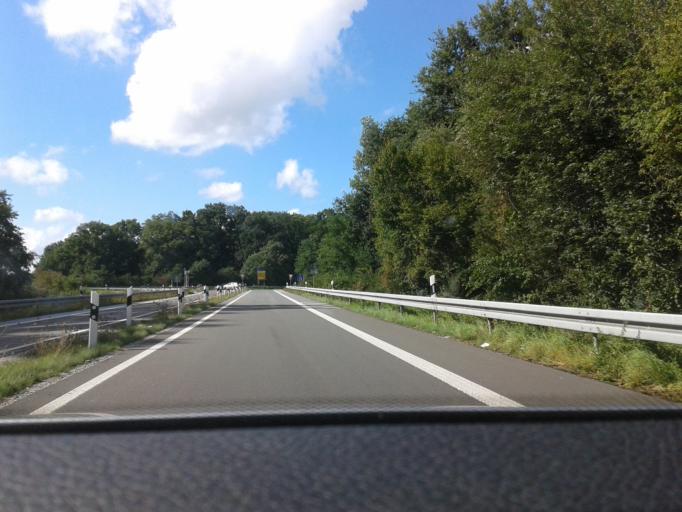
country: DE
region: North Rhine-Westphalia
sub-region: Regierungsbezirk Dusseldorf
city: Uedem
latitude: 51.6369
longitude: 6.2930
